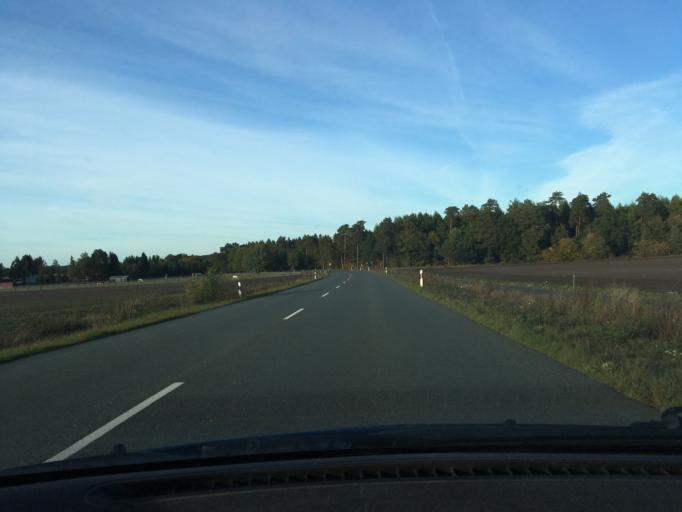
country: DE
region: Lower Saxony
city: Munster
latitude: 53.0291
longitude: 10.0585
